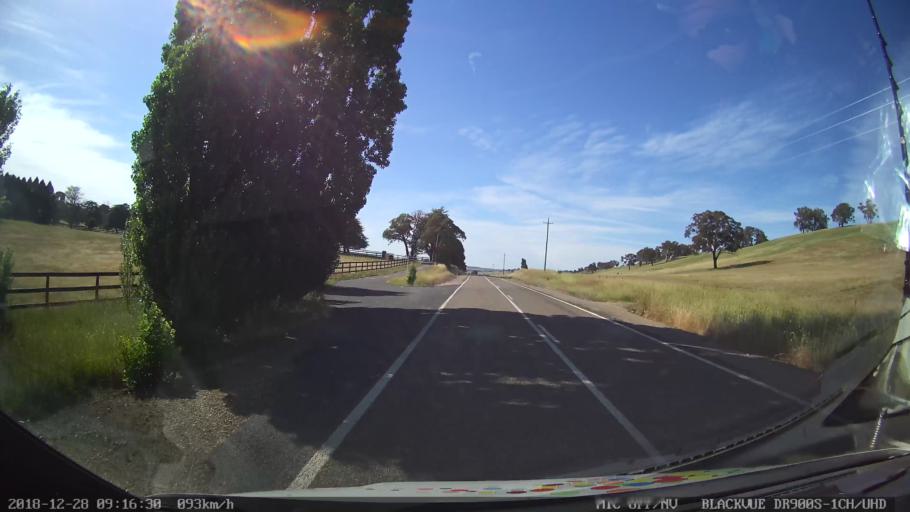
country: AU
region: New South Wales
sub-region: Upper Lachlan Shire
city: Crookwell
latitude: -34.3093
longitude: 149.3558
